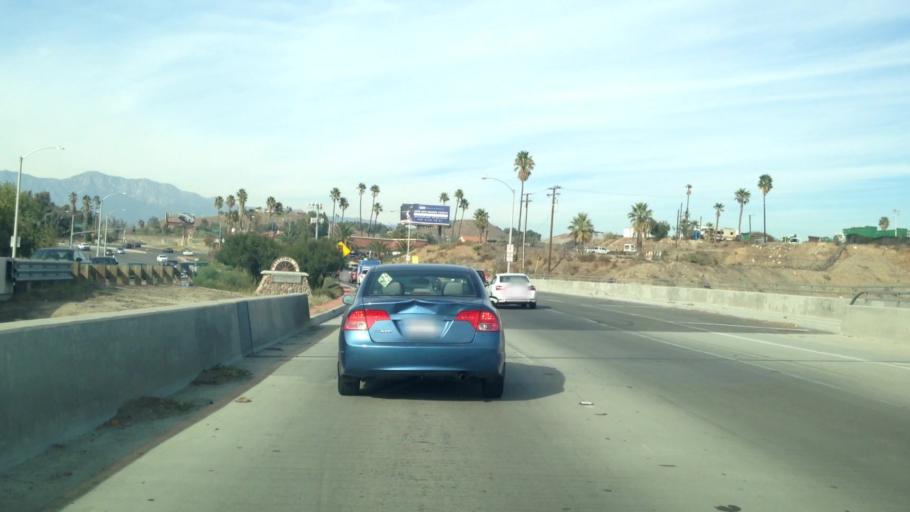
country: US
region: California
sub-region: Riverside County
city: Pedley
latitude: 33.9650
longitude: -117.4657
